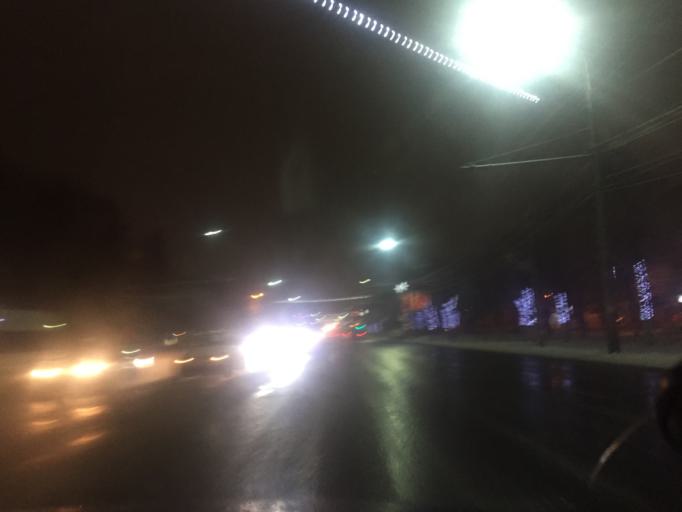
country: RU
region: Tula
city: Tula
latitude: 54.1753
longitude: 37.5979
